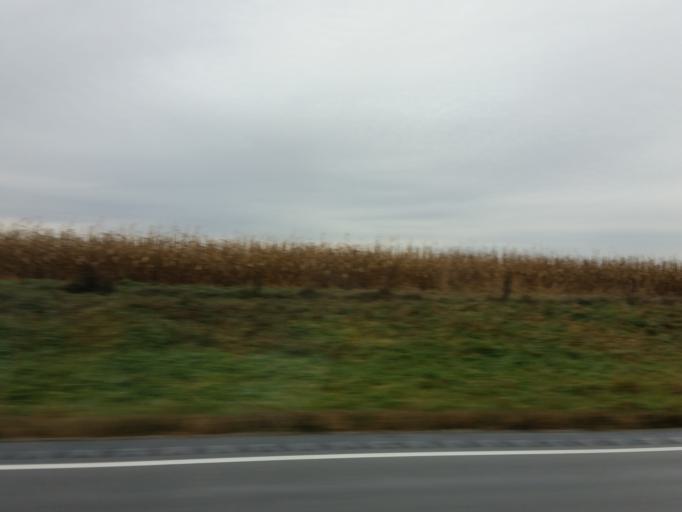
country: US
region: Iowa
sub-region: Benton County
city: Vinton
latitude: 42.0271
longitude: -92.0293
